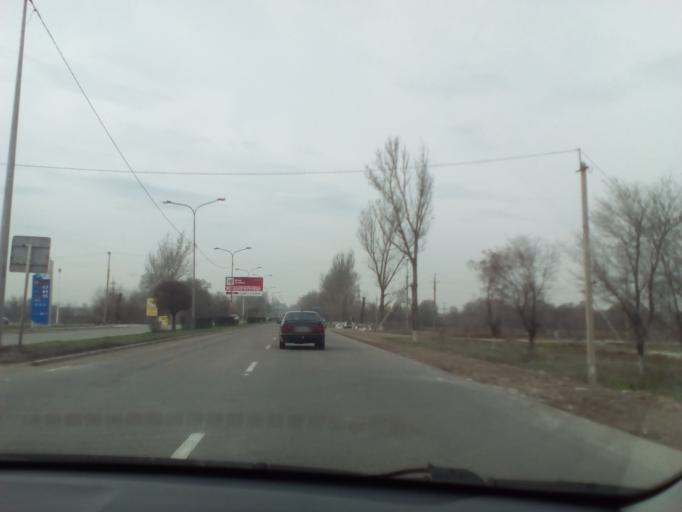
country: KZ
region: Almaty Oblysy
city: Burunday
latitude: 43.2217
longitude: 76.6224
